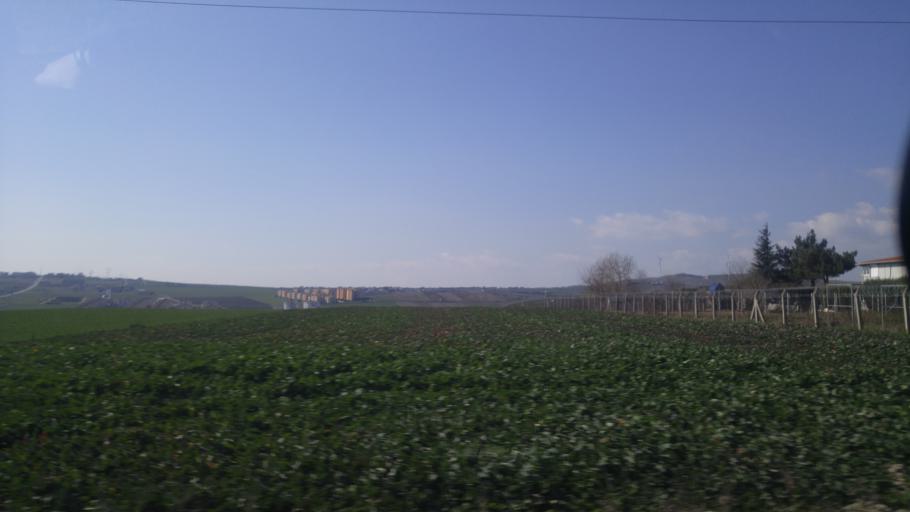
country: TR
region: Istanbul
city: Canta
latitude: 41.0944
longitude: 28.1096
